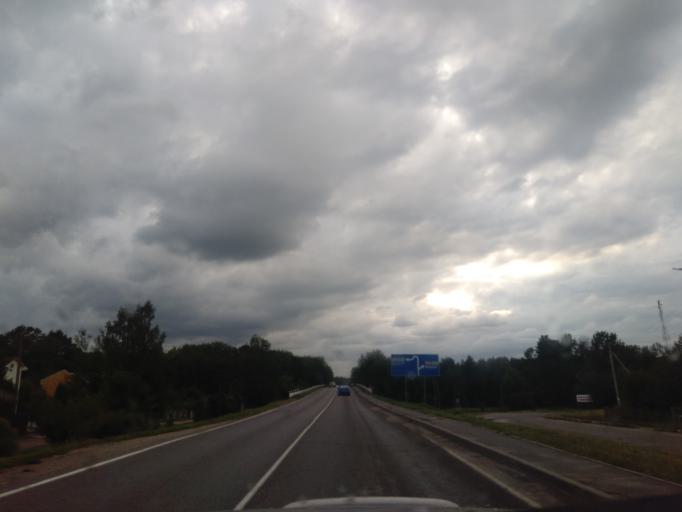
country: BY
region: Minsk
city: Enyerhyetykaw
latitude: 53.5885
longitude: 27.0494
